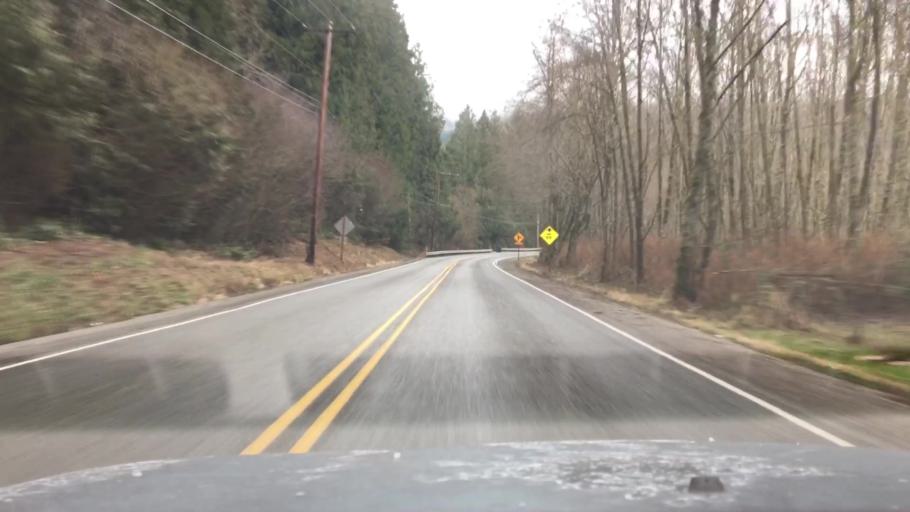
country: US
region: Washington
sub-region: Whatcom County
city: Sudden Valley
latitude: 48.6405
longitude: -122.3170
